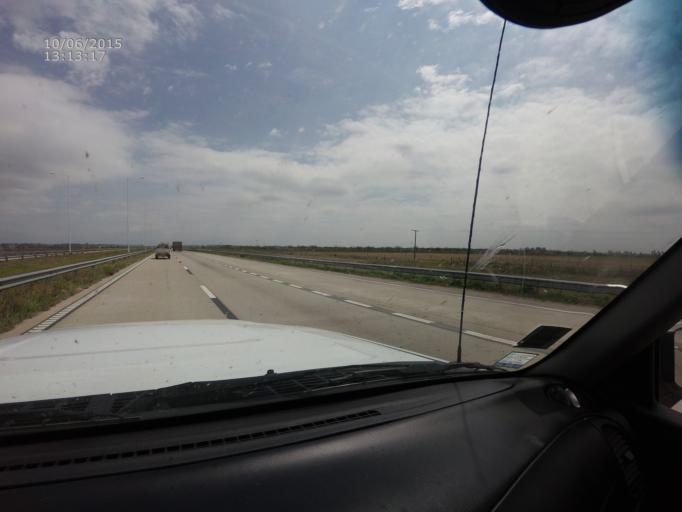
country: AR
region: Cordoba
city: General Roca
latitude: -32.7084
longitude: -61.9175
